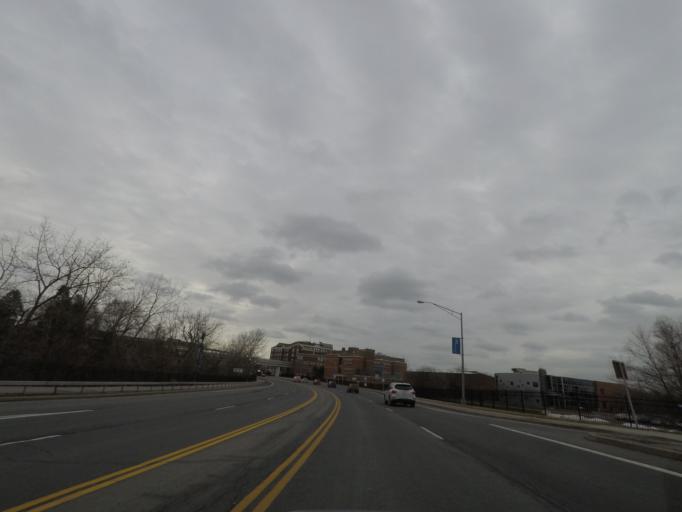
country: US
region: New York
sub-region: Schenectady County
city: Schenectady
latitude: 42.8162
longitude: -73.9524
